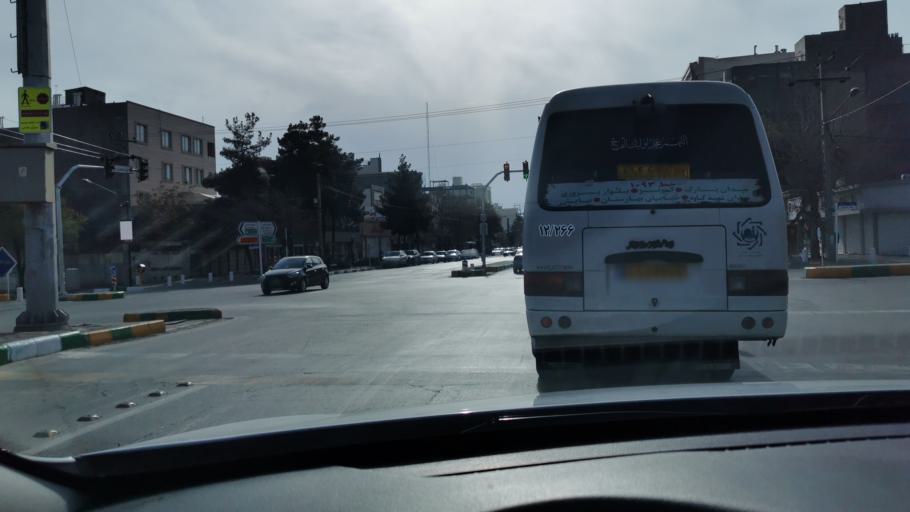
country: IR
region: Razavi Khorasan
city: Mashhad
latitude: 36.2911
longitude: 59.5376
